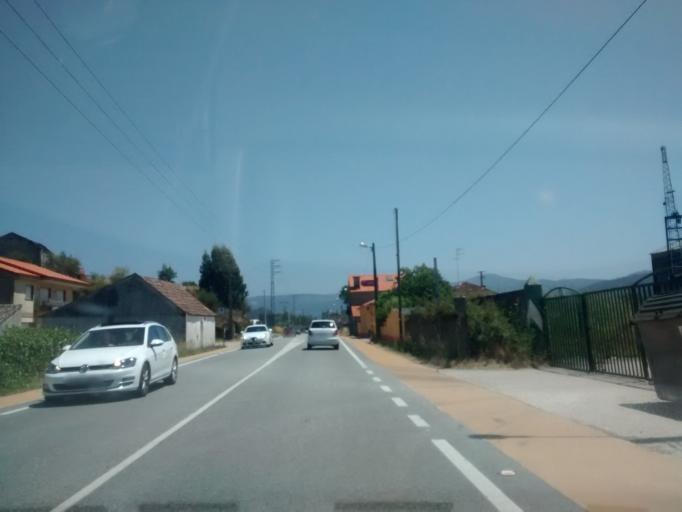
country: ES
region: Galicia
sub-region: Provincia de Pontevedra
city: Nigran
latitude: 42.1148
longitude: -8.8034
